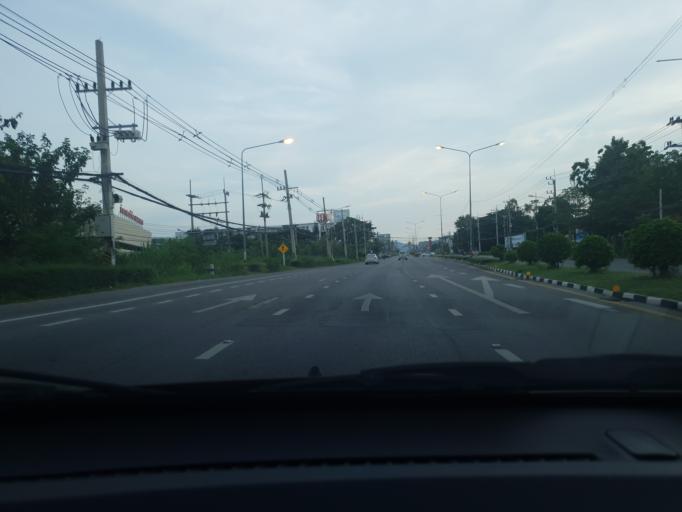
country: TH
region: Prachuap Khiri Khan
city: Hua Hin
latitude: 12.6283
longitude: 99.9510
